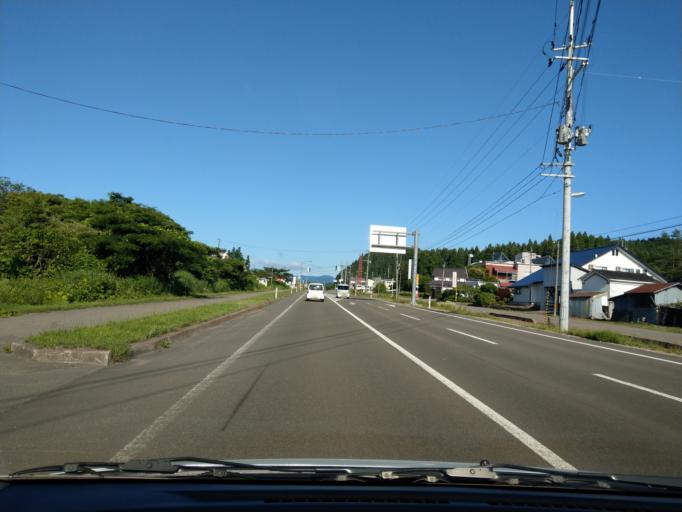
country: JP
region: Akita
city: Takanosu
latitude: 40.1196
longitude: 140.3794
